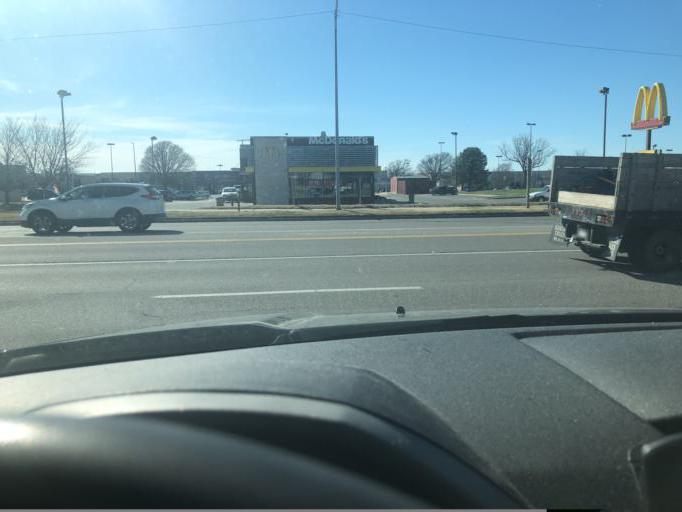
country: US
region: Kansas
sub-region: Sedgwick County
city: Bellaire
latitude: 37.7475
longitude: -97.2446
